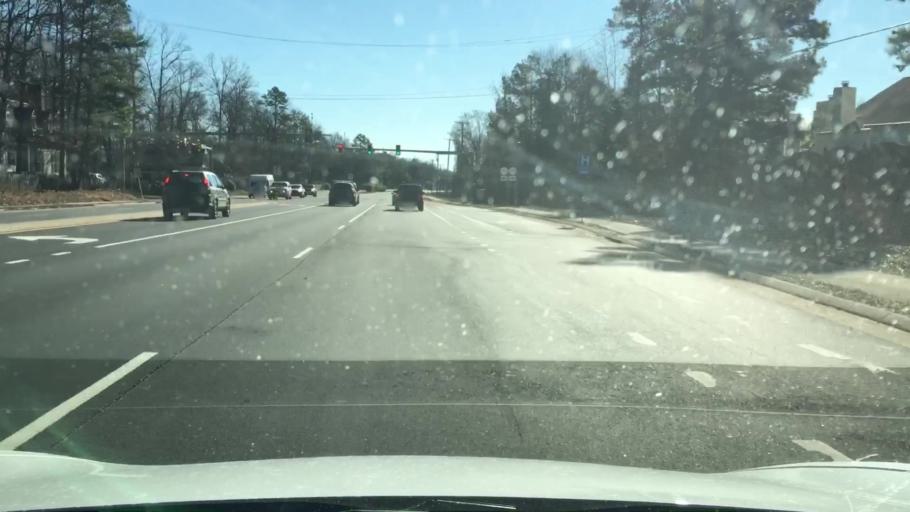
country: US
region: Virginia
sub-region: Chesterfield County
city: Bon Air
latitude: 37.5147
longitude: -77.5917
